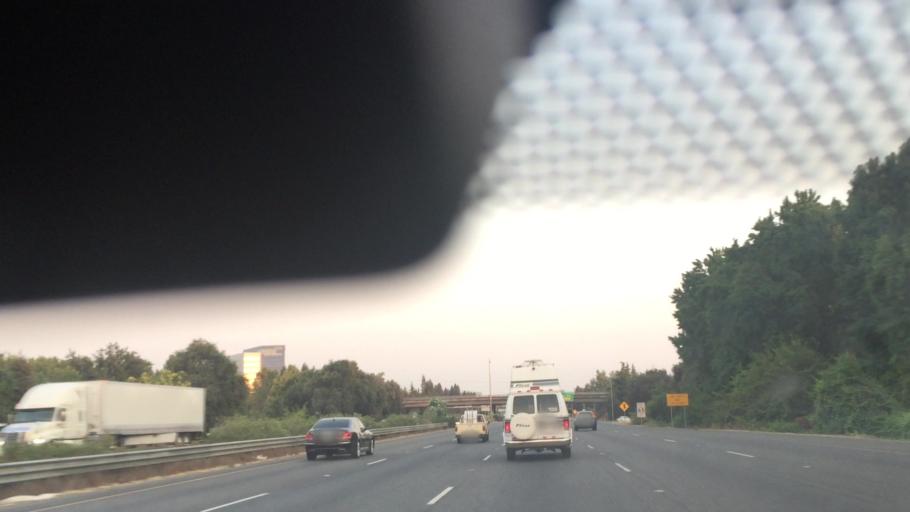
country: US
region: California
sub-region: Yolo County
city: West Sacramento
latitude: 38.6171
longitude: -121.5137
